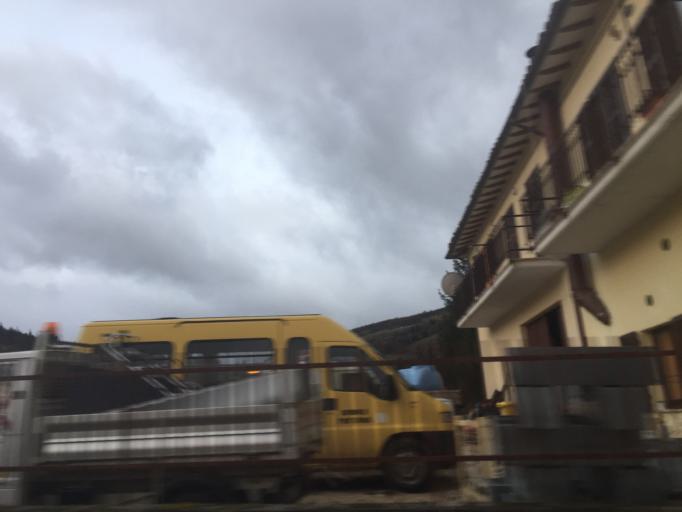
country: IT
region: The Marches
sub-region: Provincia di Macerata
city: Pieve Torina
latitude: 43.0402
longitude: 13.0488
